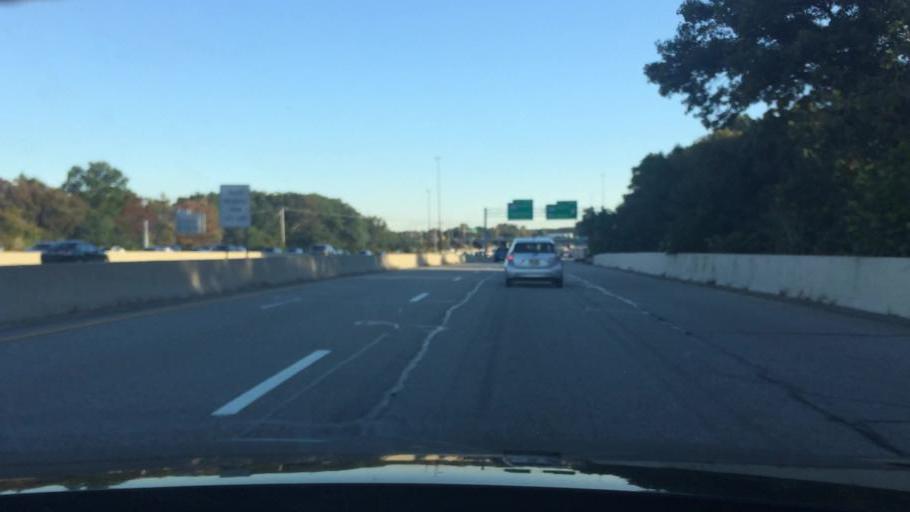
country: US
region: Massachusetts
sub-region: Middlesex County
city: Lowell
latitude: 42.6123
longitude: -71.3283
